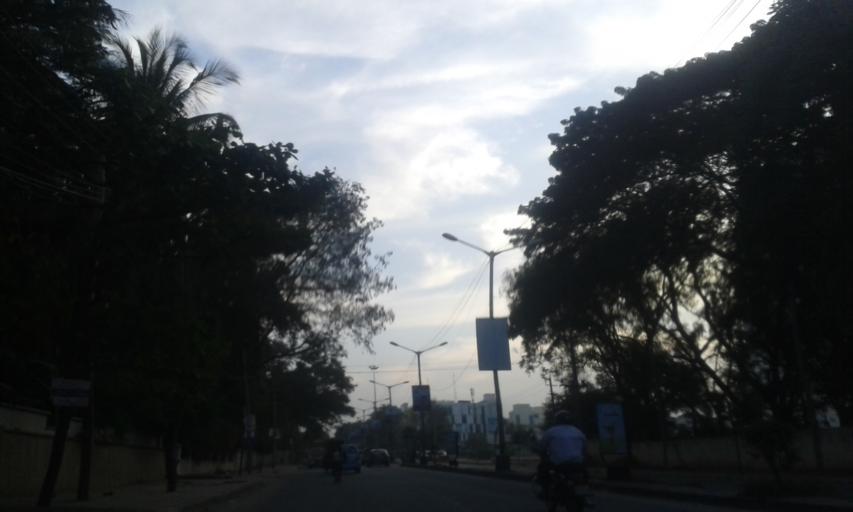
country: IN
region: Karnataka
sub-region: Bangalore Rural
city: Hoskote
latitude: 12.9859
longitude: 77.7533
